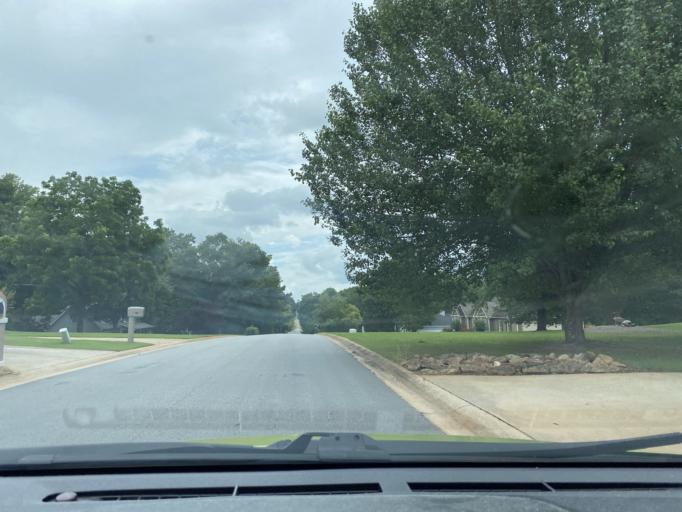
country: US
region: Georgia
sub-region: Fulton County
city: Palmetto
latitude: 33.4281
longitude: -84.6828
